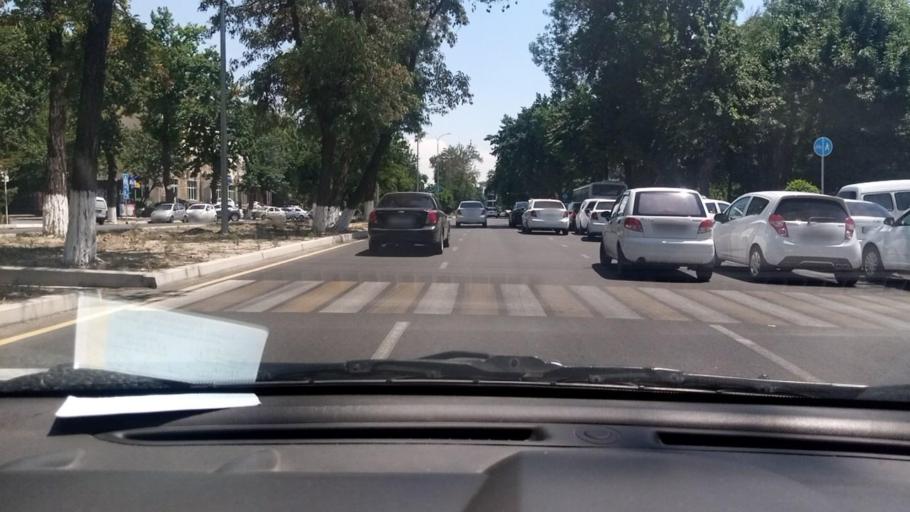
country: UZ
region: Toshkent Shahri
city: Tashkent
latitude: 41.2914
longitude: 69.1997
